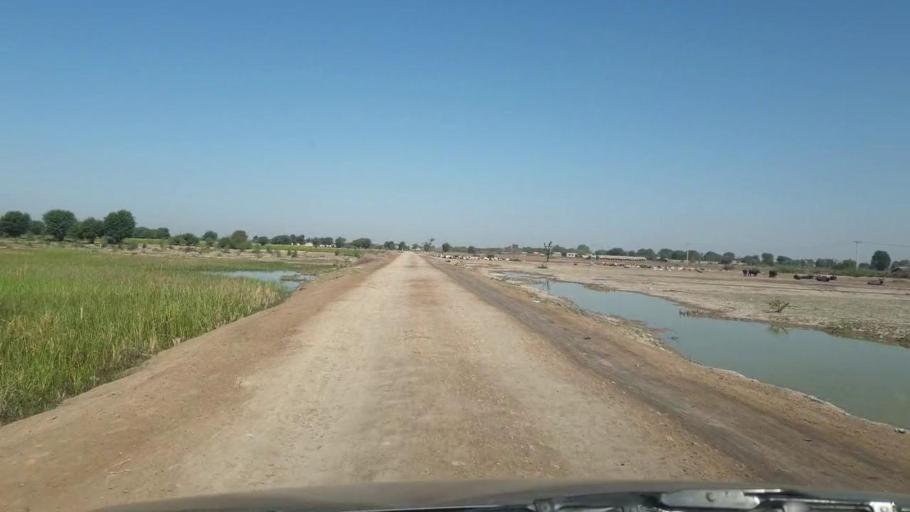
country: PK
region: Sindh
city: Umarkot
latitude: 25.3866
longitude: 69.6611
